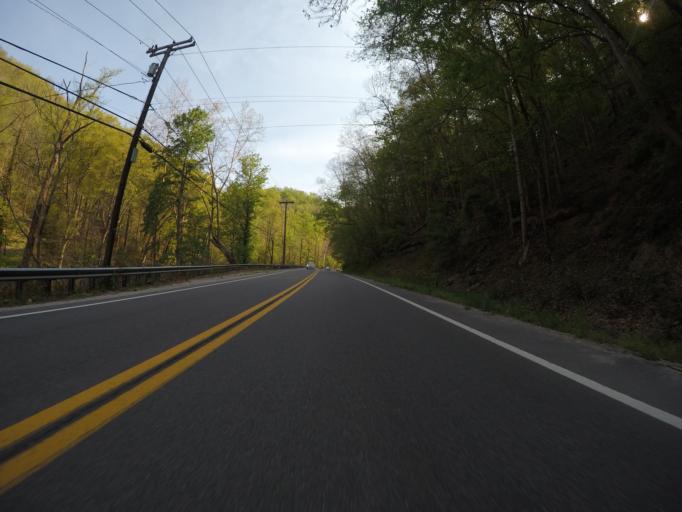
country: US
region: West Virginia
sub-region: Kanawha County
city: Charleston
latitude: 38.3628
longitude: -81.5852
